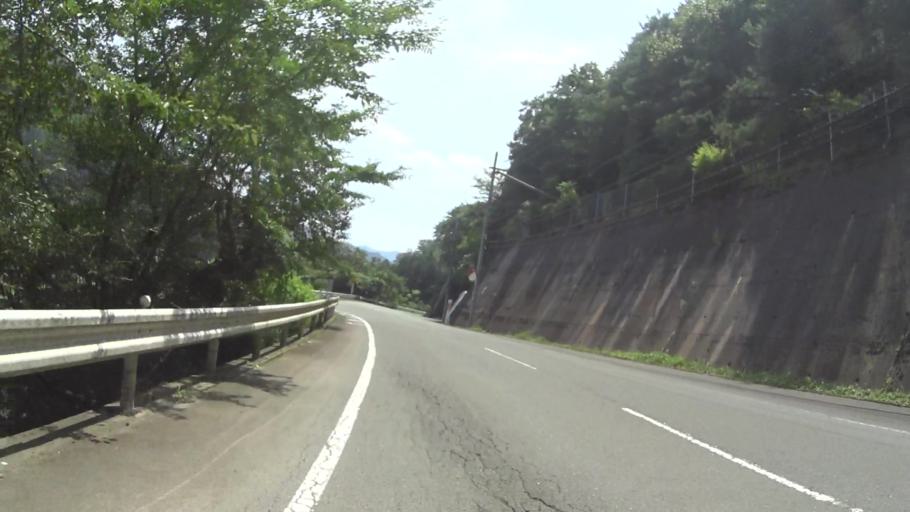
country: JP
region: Kyoto
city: Ayabe
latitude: 35.2824
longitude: 135.4295
